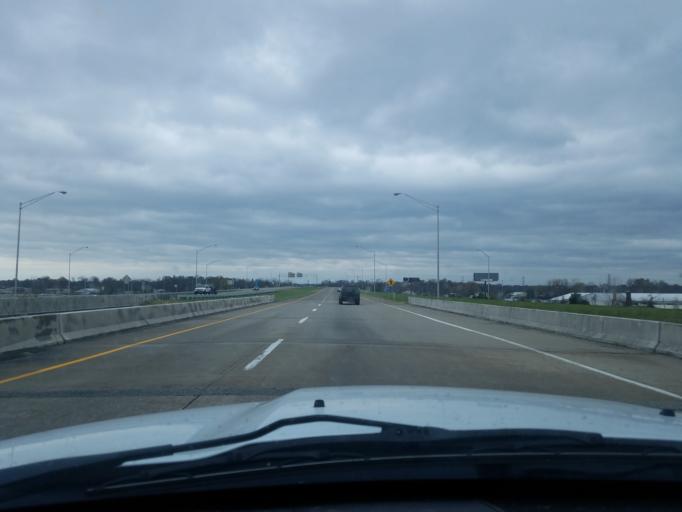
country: US
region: Indiana
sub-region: Clark County
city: Clarksville
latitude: 38.3457
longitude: -85.7521
